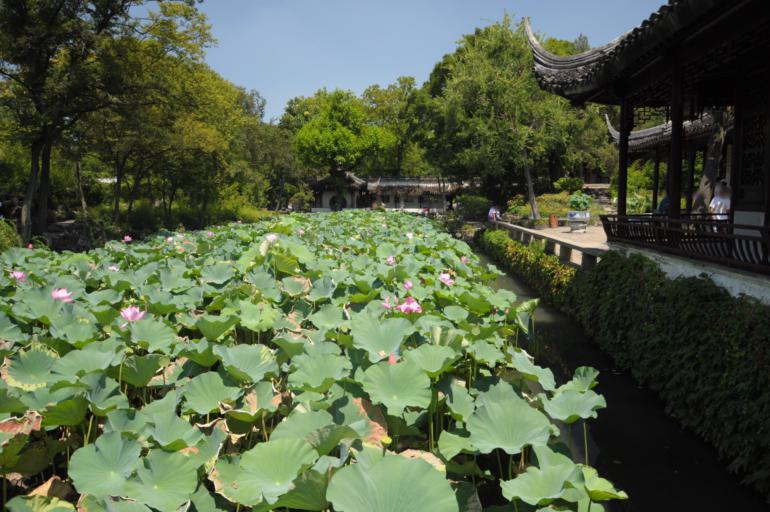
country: CN
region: Jiangsu Sheng
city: Pingjianglu
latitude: 31.3264
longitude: 120.6243
